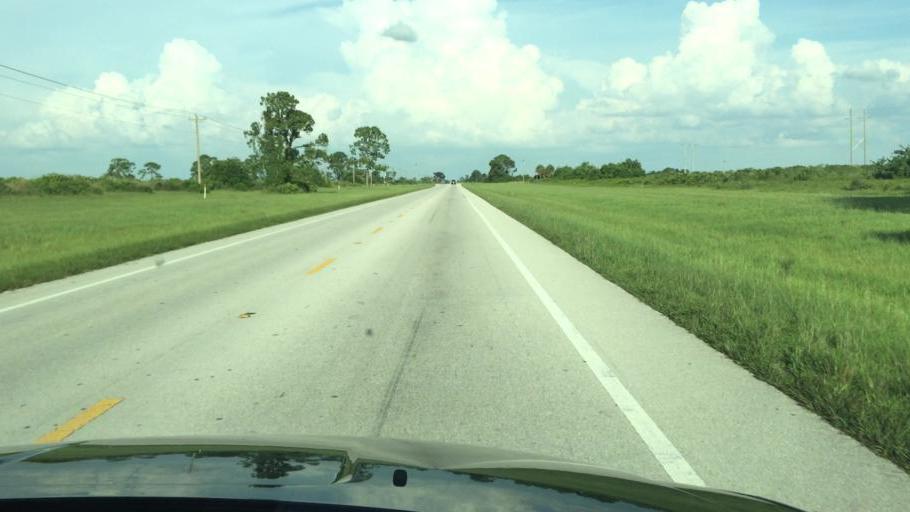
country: US
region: Florida
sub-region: Collier County
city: Immokalee
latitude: 26.4978
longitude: -81.4859
